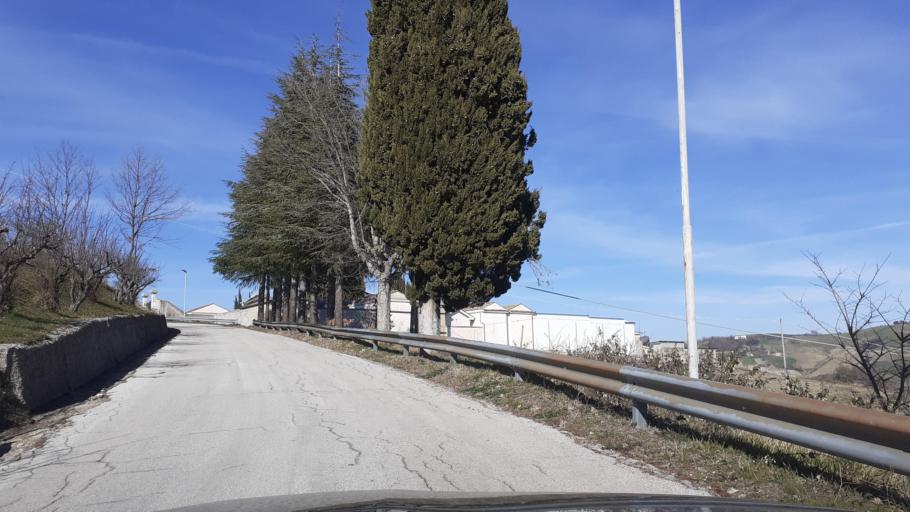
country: IT
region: Molise
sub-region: Provincia di Campobasso
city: Pietracupa
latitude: 41.6841
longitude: 14.5231
